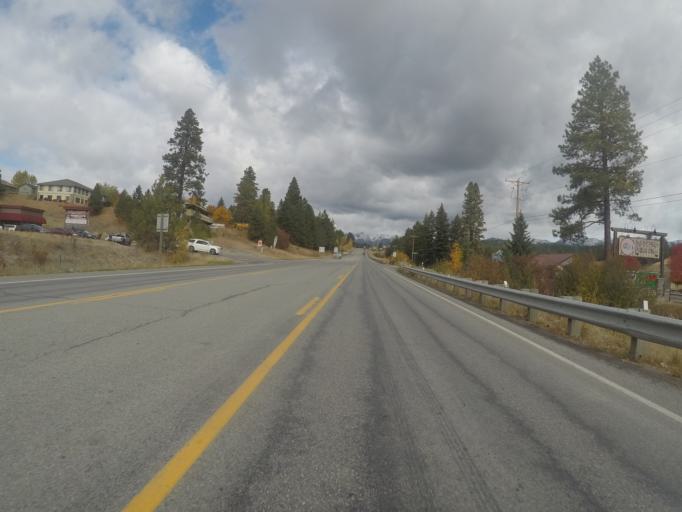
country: US
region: Montana
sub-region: Flathead County
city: Bigfork
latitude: 48.0674
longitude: -114.0813
